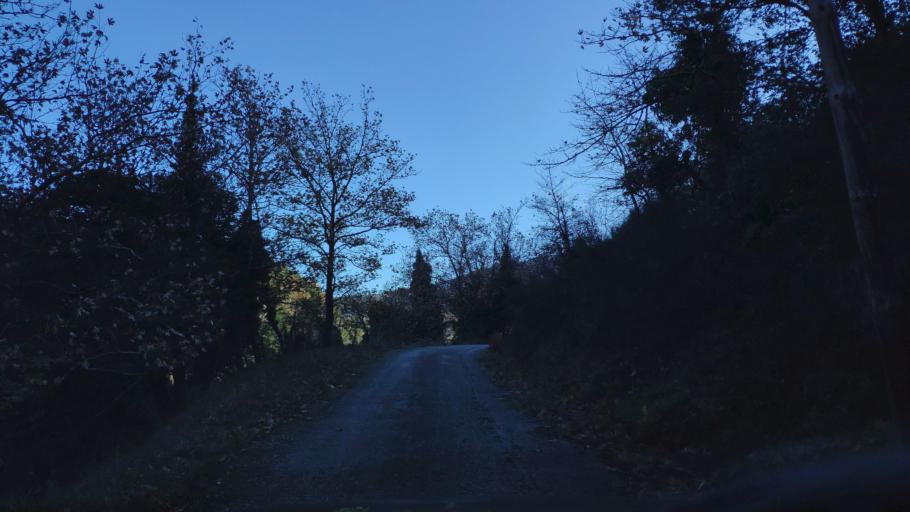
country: GR
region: West Greece
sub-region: Nomos Achaias
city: Aiyira
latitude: 38.0492
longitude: 22.4483
